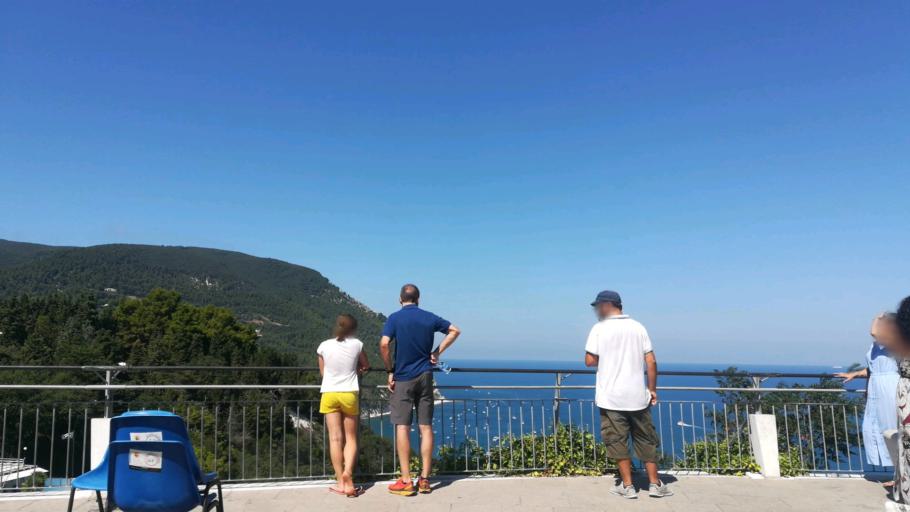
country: IT
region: The Marches
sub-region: Provincia di Ancona
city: Sirolo
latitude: 43.5232
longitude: 13.6201
